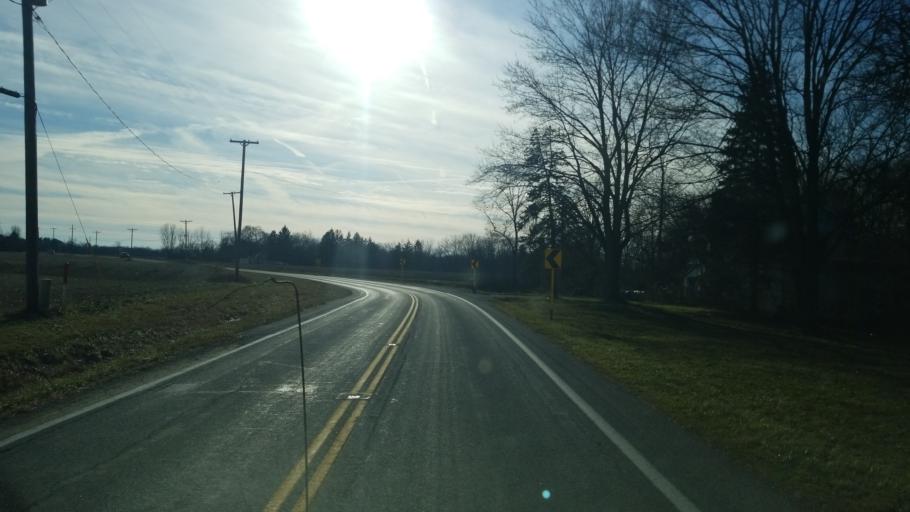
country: US
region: Ohio
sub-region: Sandusky County
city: Green Springs
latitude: 41.2924
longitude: -83.0516
